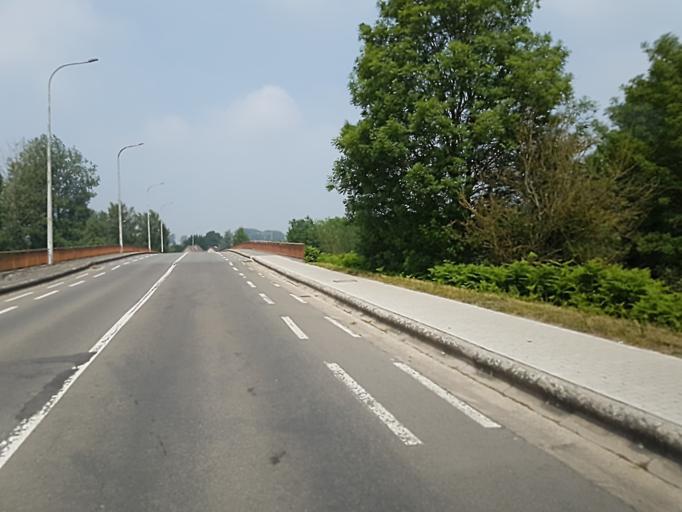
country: BE
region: Flanders
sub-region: Provincie Oost-Vlaanderen
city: Geraardsbergen
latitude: 50.7927
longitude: 3.9020
